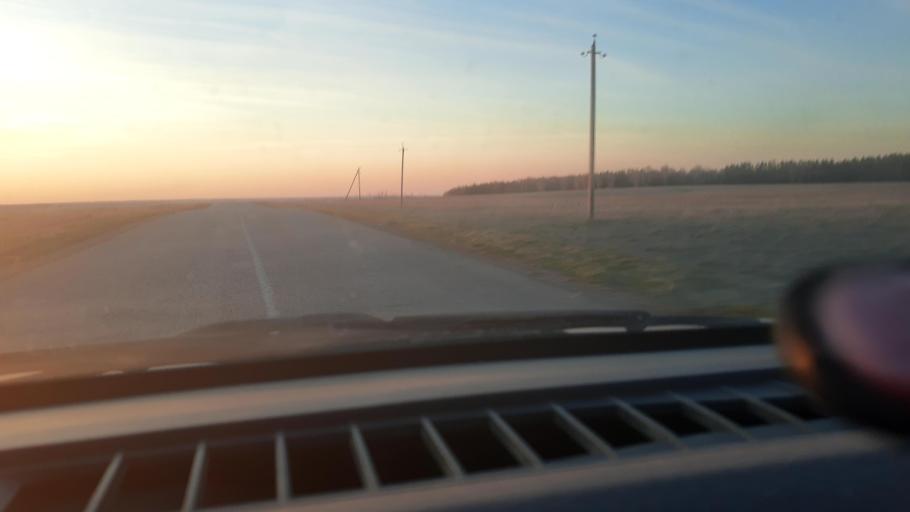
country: RU
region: Bashkortostan
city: Asanovo
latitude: 54.8169
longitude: 55.4780
